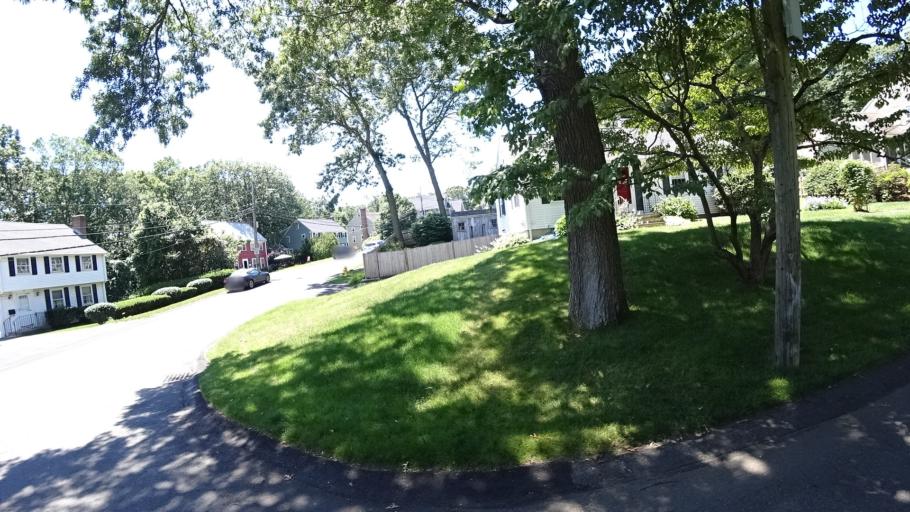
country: US
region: Massachusetts
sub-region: Norfolk County
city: Dedham
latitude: 42.2221
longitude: -71.1591
